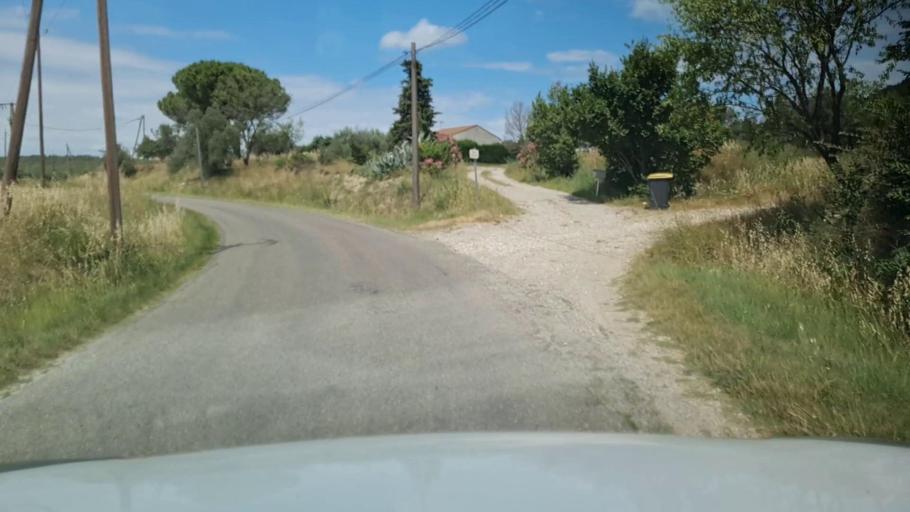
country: FR
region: Languedoc-Roussillon
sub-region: Departement du Gard
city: Clarensac
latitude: 43.8267
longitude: 4.1923
